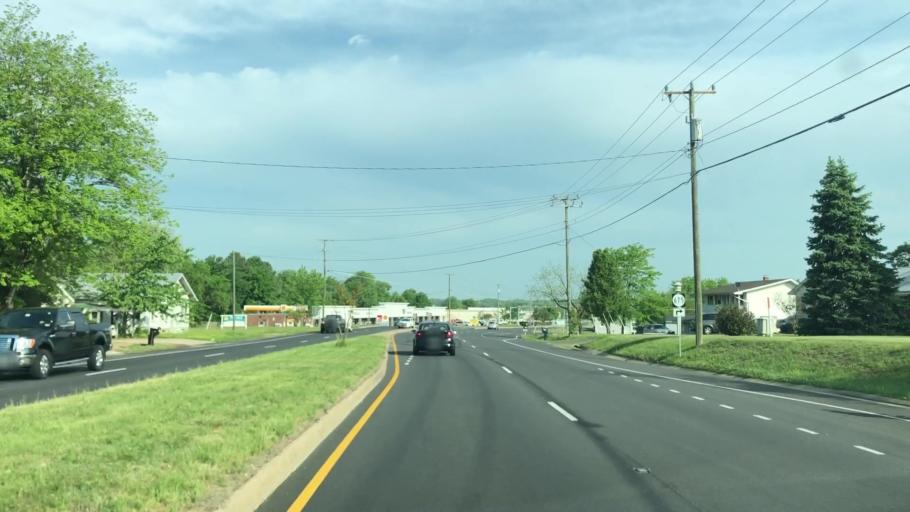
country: US
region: Virginia
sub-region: Stafford County
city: Stafford
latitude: 38.4731
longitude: -77.4677
